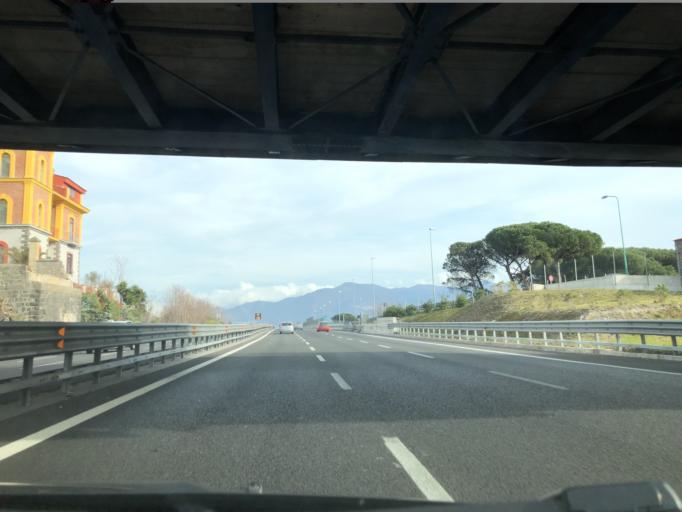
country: IT
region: Campania
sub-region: Provincia di Napoli
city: Trecase
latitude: 40.7697
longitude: 14.4198
